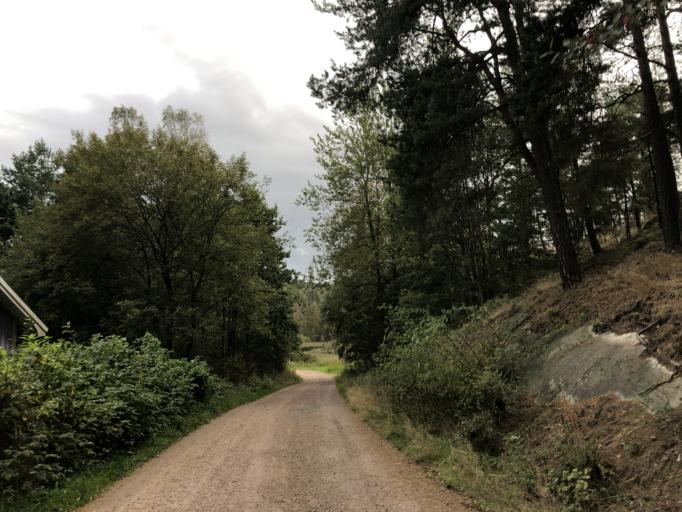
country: SE
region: Vaestra Goetaland
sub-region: Goteborg
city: Majorna
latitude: 57.7446
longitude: 11.8987
